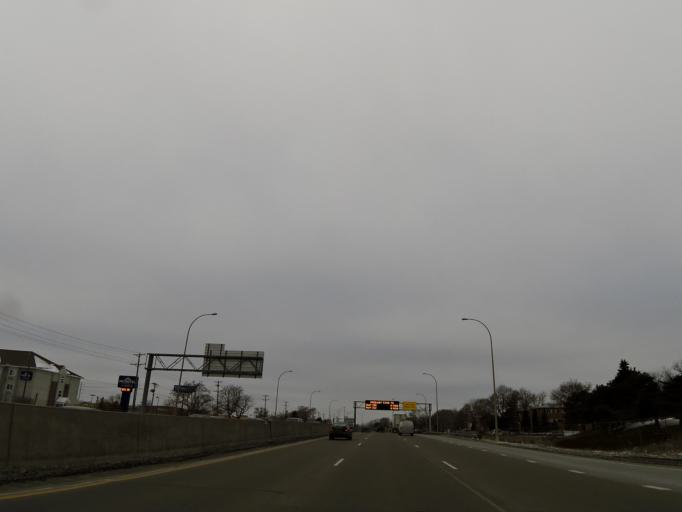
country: US
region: Minnesota
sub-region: Hennepin County
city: Richfield
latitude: 44.8623
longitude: -93.2613
